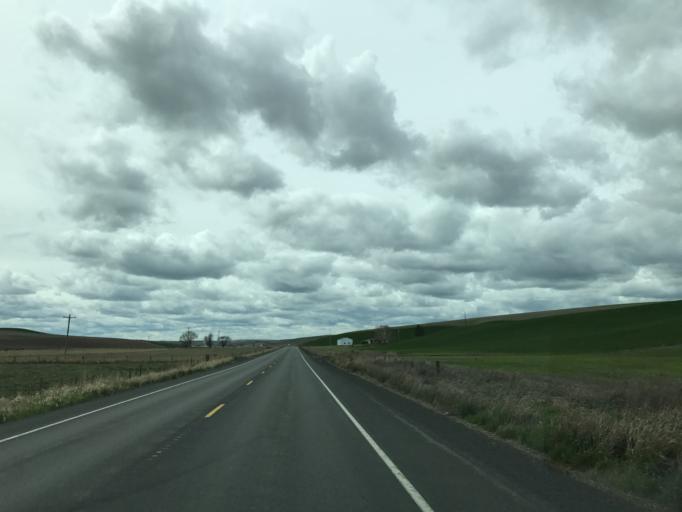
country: US
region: Washington
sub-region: Whitman County
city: Colfax
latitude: 46.8135
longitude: -117.5968
